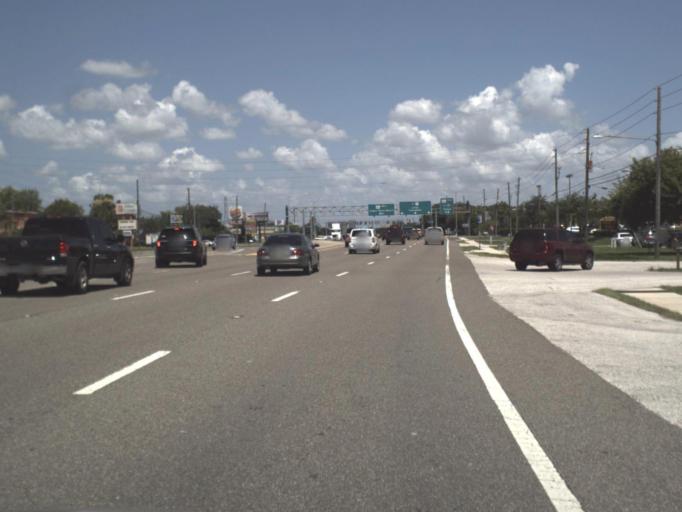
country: US
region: Florida
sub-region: Pinellas County
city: South Highpoint
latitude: 27.8899
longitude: -82.7290
